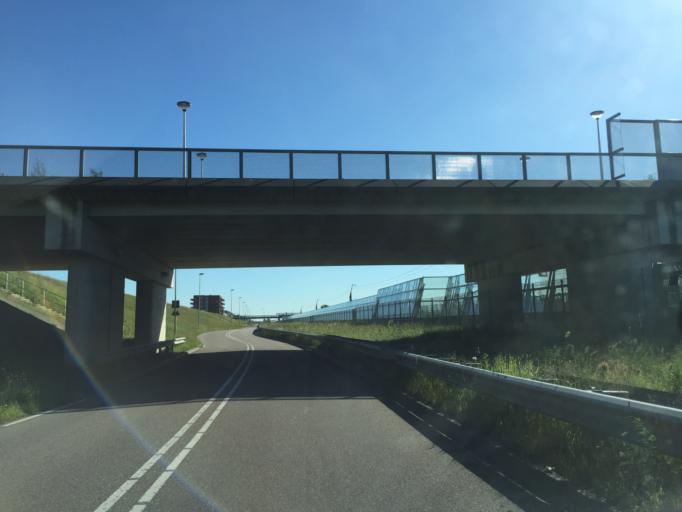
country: NL
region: South Holland
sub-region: Gemeente Lansingerland
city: Bergschenhoek
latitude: 52.0007
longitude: 4.4979
